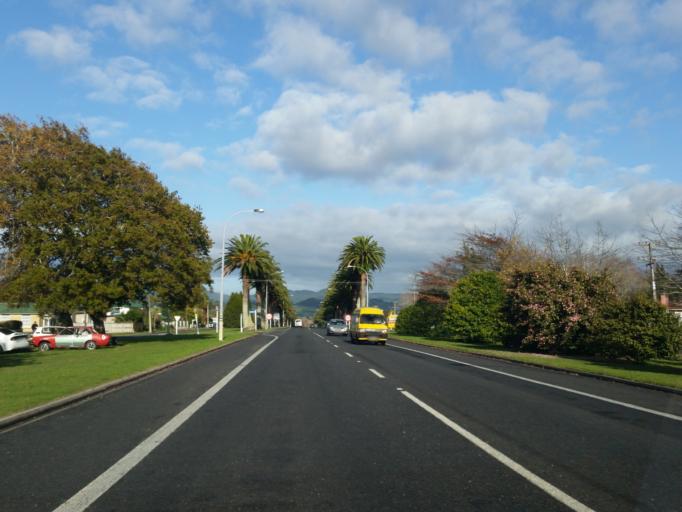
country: NZ
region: Waikato
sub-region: Hauraki District
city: Waihi
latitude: -37.3953
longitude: 175.8297
